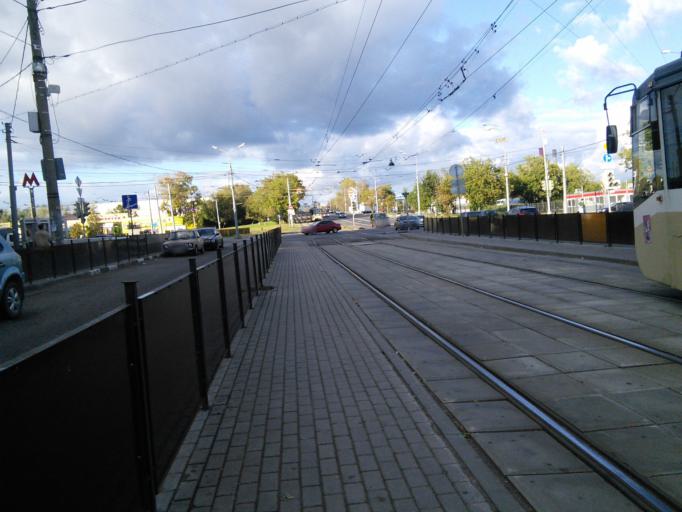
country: RU
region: Moskovskaya
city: Bogorodskoye
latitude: 55.8130
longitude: 37.7350
